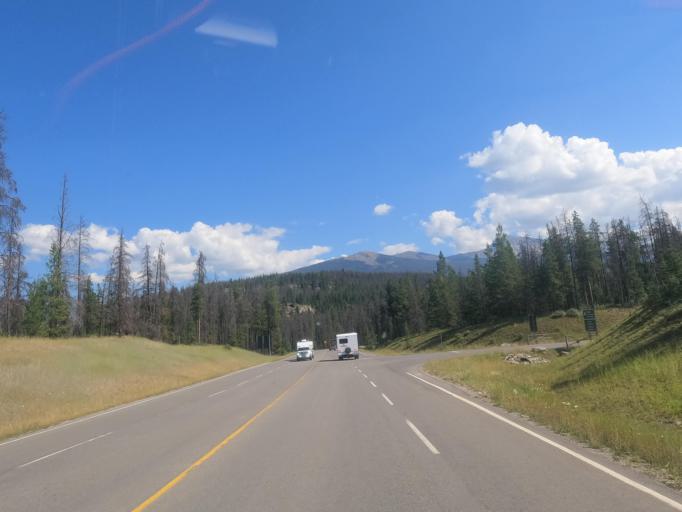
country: CA
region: Alberta
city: Jasper Park Lodge
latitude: 52.8542
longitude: -118.0800
